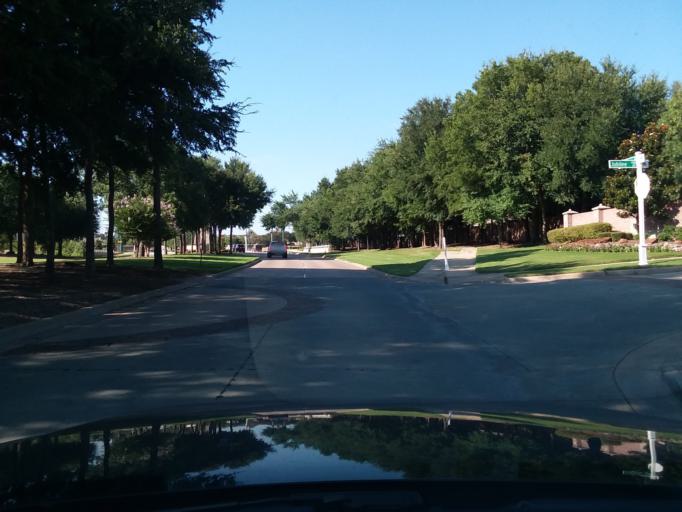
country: US
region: Texas
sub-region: Denton County
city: Double Oak
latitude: 33.0432
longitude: -97.0947
